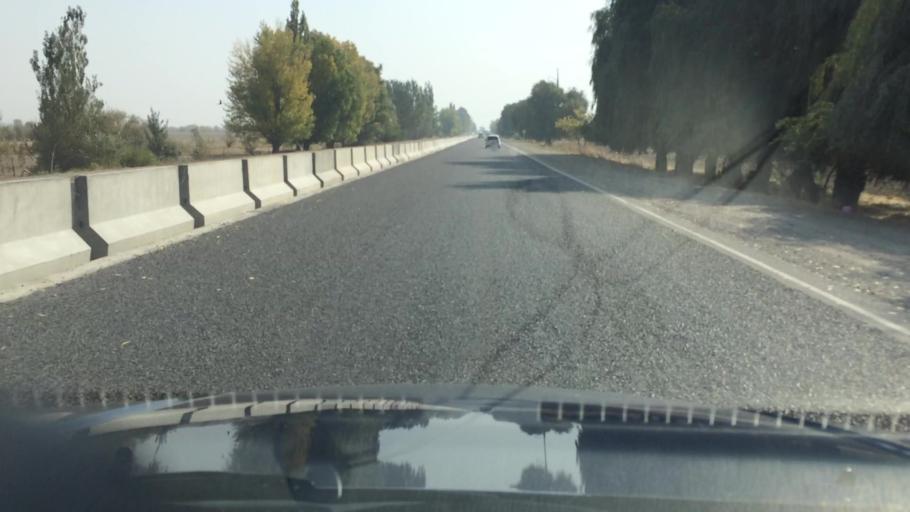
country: KG
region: Chuy
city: Kant
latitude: 42.9689
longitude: 74.9057
